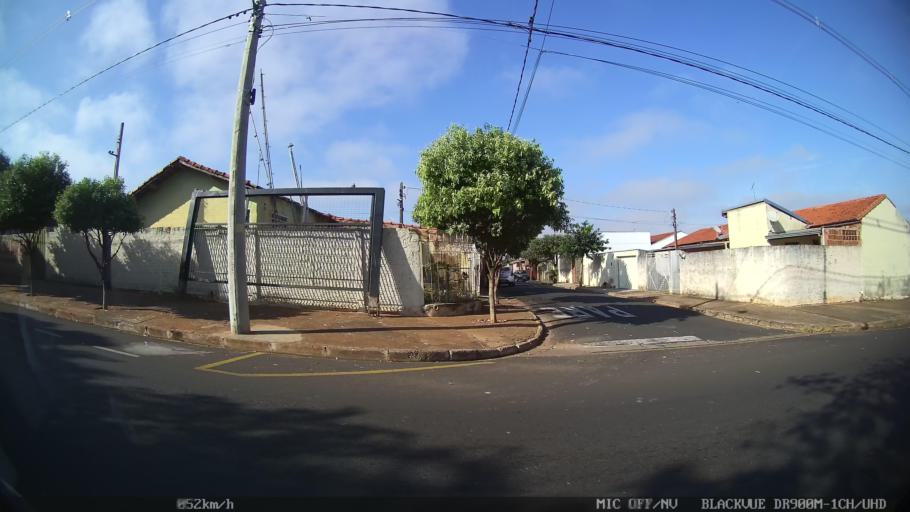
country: BR
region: Sao Paulo
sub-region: Sao Jose Do Rio Preto
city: Sao Jose do Rio Preto
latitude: -20.7932
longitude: -49.4207
